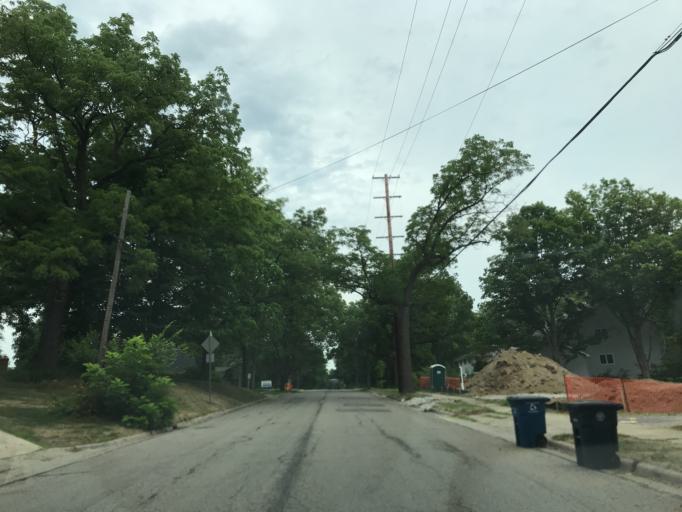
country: US
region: Michigan
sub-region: Washtenaw County
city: Ann Arbor
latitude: 42.2952
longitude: -83.7352
